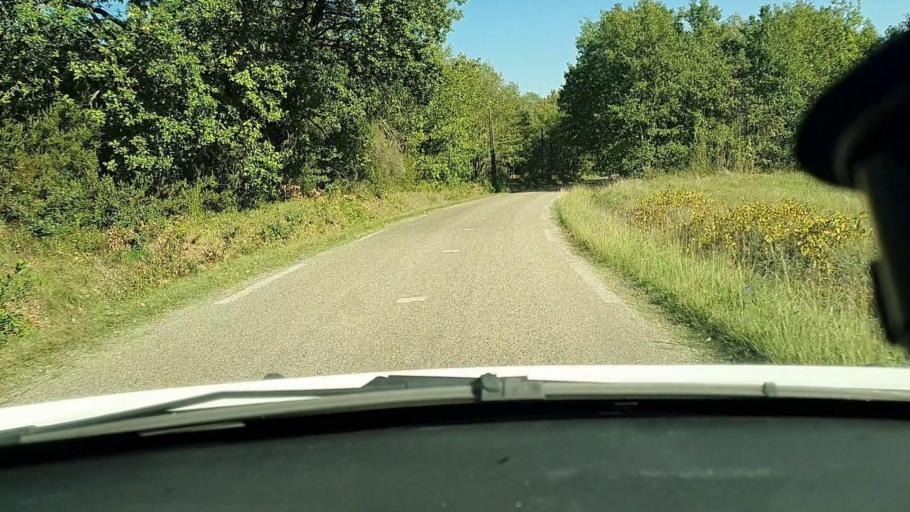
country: FR
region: Languedoc-Roussillon
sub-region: Departement du Gard
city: Saint-Julien-de-Peyrolas
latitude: 44.2739
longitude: 4.5353
